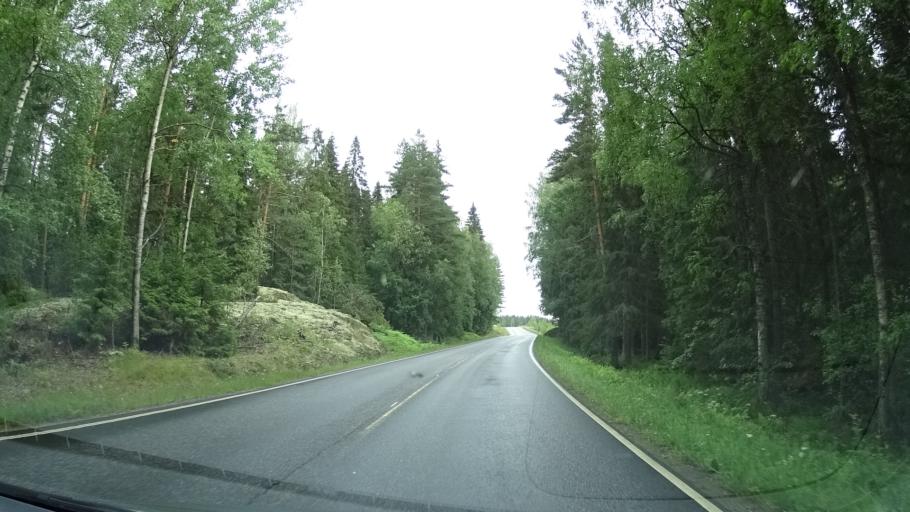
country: FI
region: Haeme
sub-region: Forssa
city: Humppila
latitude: 61.0973
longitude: 23.3450
